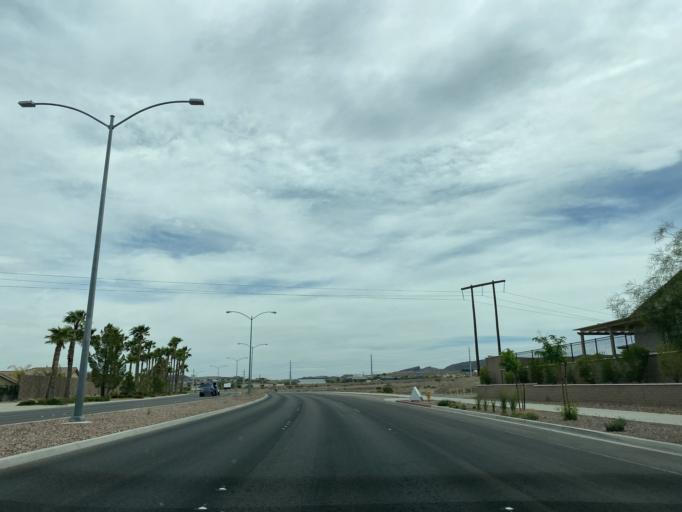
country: US
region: Nevada
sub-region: Clark County
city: Henderson
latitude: 36.0713
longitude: -114.9626
